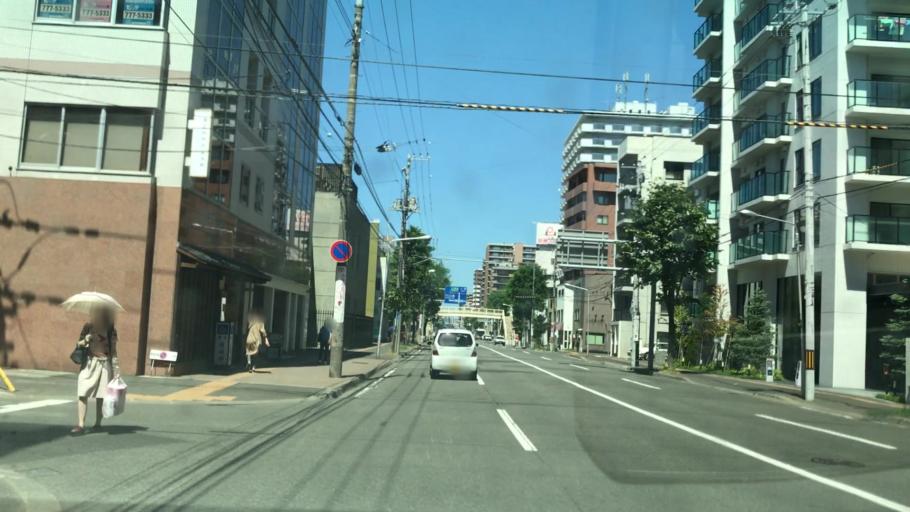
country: JP
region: Hokkaido
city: Sapporo
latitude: 43.0566
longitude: 141.3202
